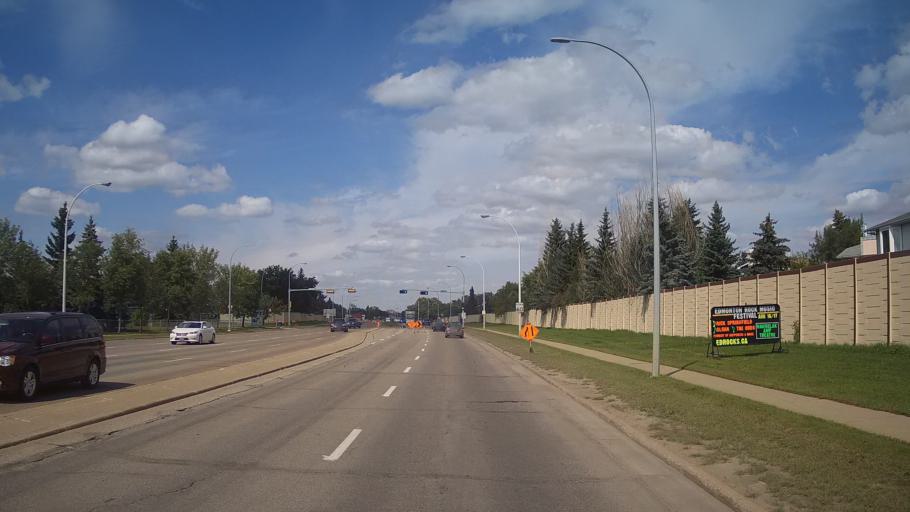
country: CA
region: Alberta
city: St. Albert
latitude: 53.5250
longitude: -113.6299
